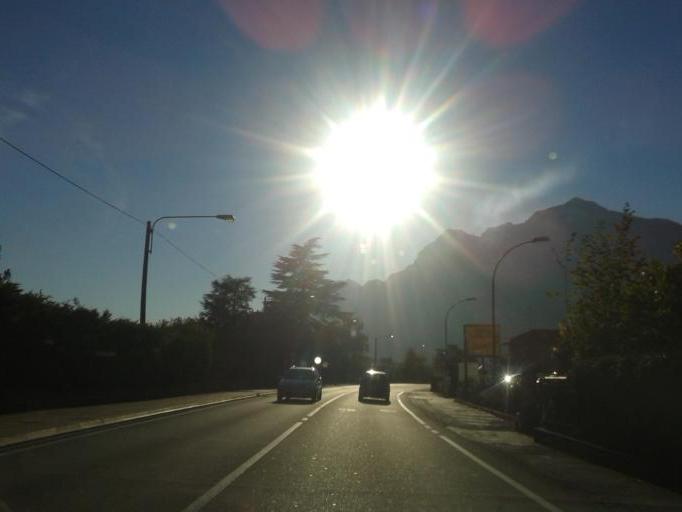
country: IT
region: Trentino-Alto Adige
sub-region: Provincia di Trento
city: Arco
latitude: 45.9121
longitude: 10.8750
